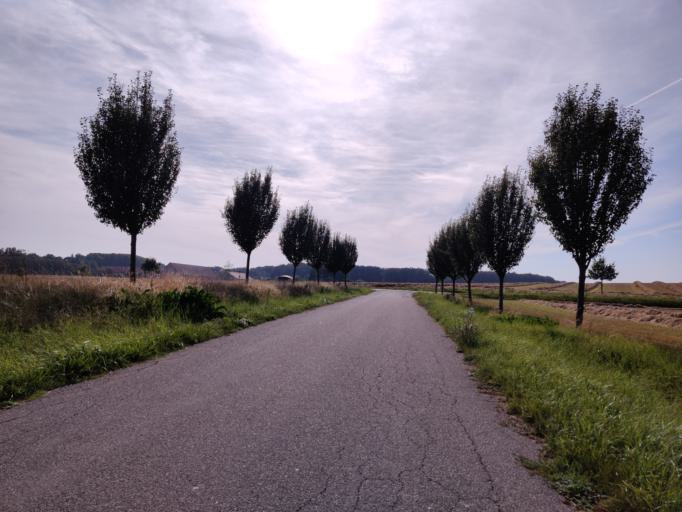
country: DK
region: Zealand
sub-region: Guldborgsund Kommune
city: Nykobing Falster
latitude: 54.6524
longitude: 11.8888
